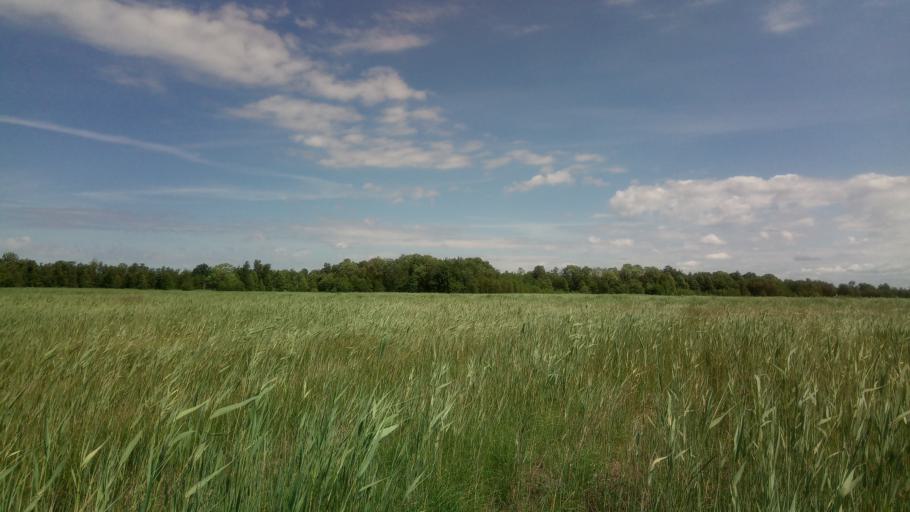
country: LT
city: Priekule
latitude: 55.5384
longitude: 21.2190
